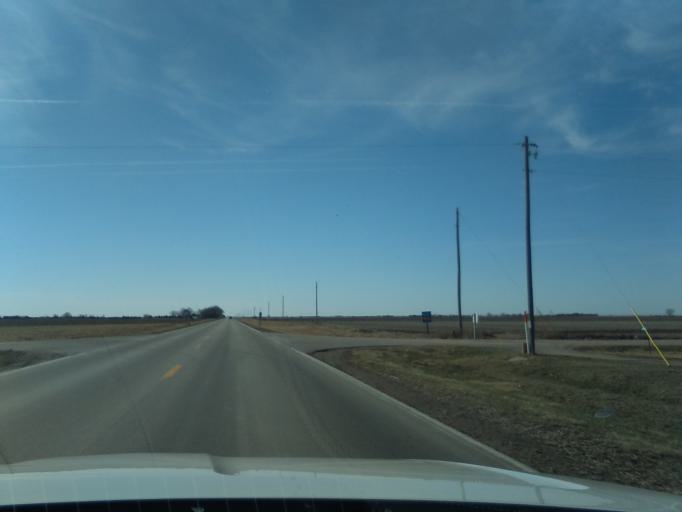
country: US
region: Nebraska
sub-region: Saline County
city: Friend
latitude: 40.8149
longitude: -97.2921
